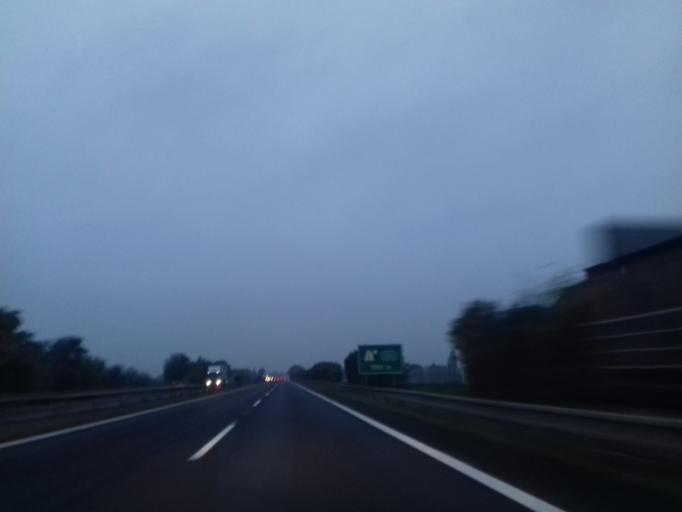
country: CZ
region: Olomoucky
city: Naklo
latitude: 49.6564
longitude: 17.1141
